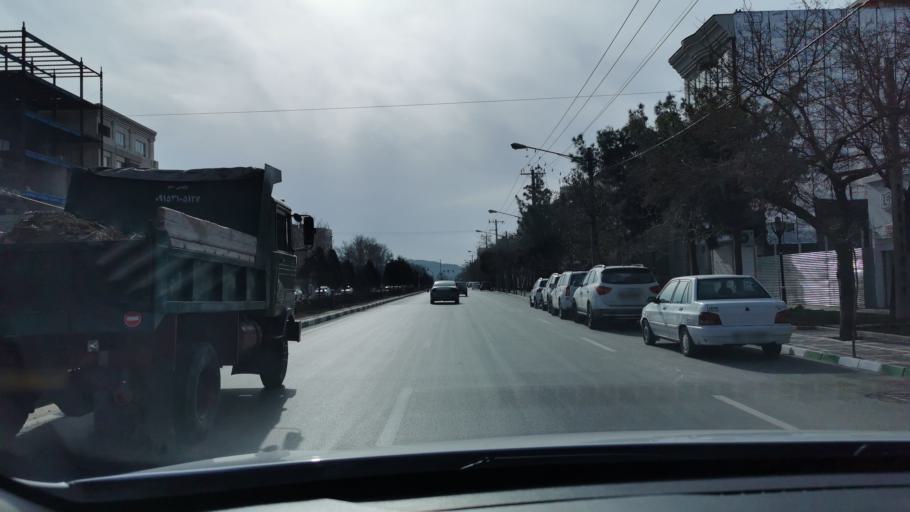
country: IR
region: Razavi Khorasan
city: Mashhad
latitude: 36.2888
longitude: 59.5414
